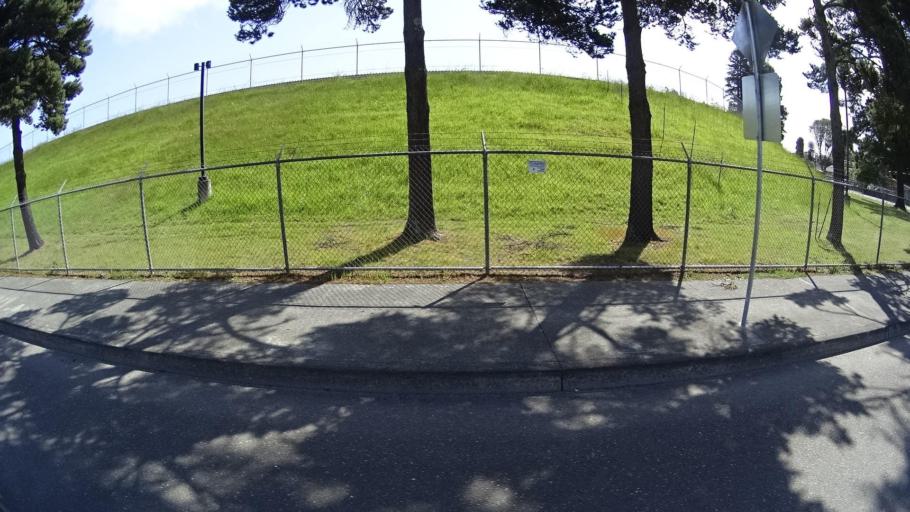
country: US
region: California
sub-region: Humboldt County
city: Cutten
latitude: 40.7737
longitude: -124.1445
